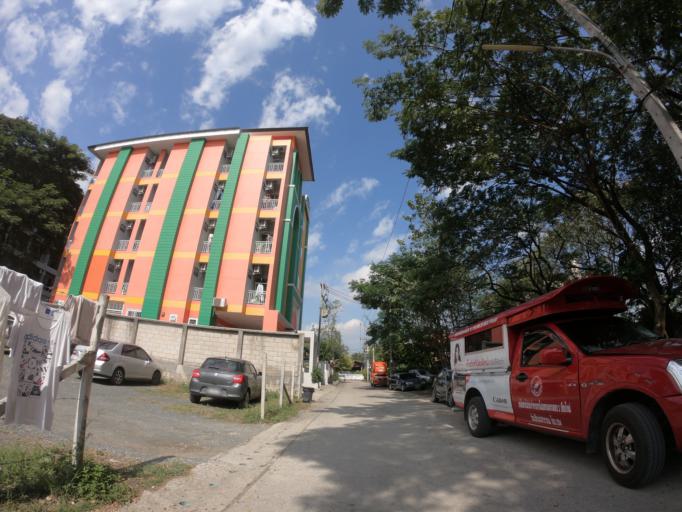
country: TH
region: Chiang Mai
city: Chiang Mai
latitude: 18.7717
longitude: 98.9869
